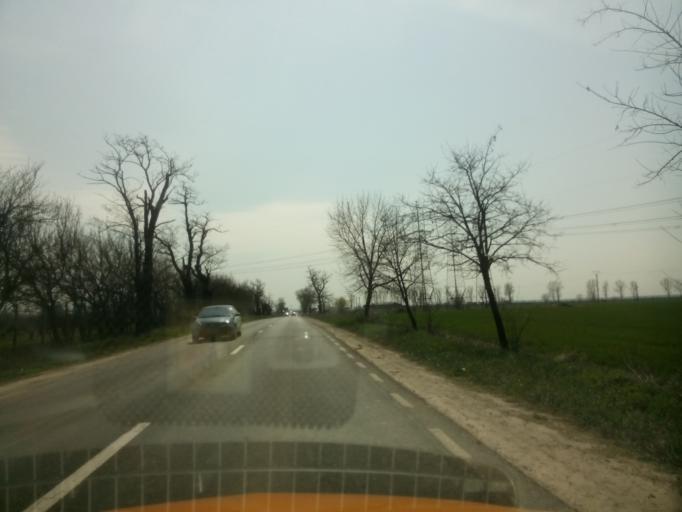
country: RO
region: Giurgiu
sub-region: Comuna Herasti
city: Herasti
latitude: 44.2536
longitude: 26.3659
